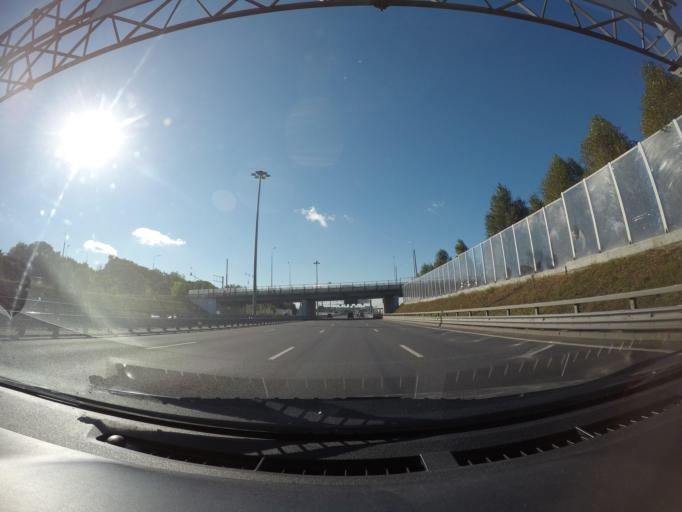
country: RU
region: Moscow
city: Ryazanskiy
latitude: 55.7696
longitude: 37.7467
